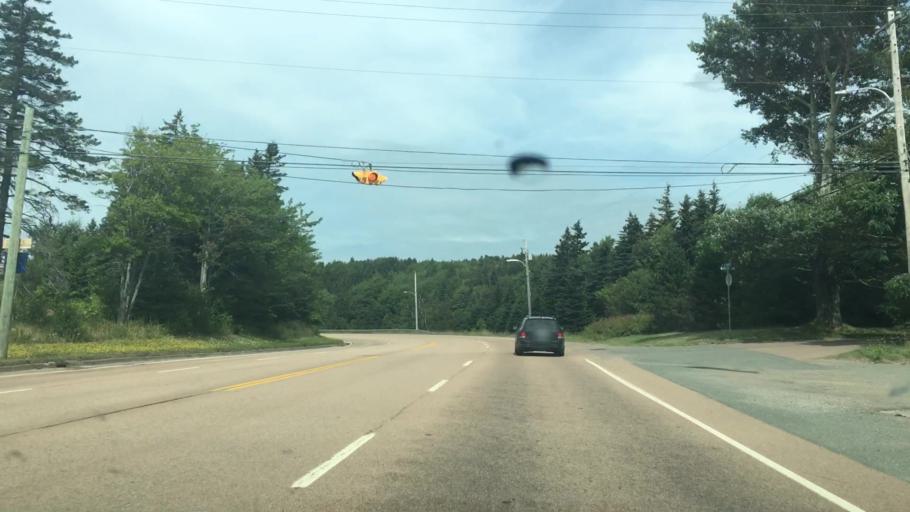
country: CA
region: Nova Scotia
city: Port Hawkesbury
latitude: 45.6236
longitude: -61.3651
